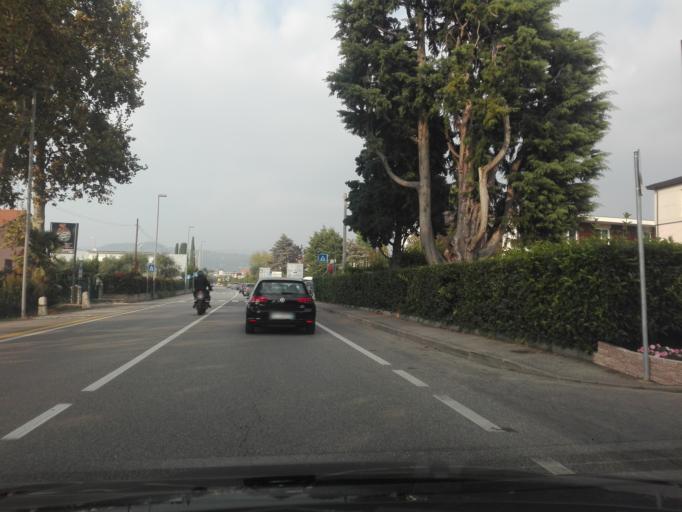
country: IT
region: Veneto
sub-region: Provincia di Verona
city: Bardolino
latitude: 45.5348
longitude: 10.7275
